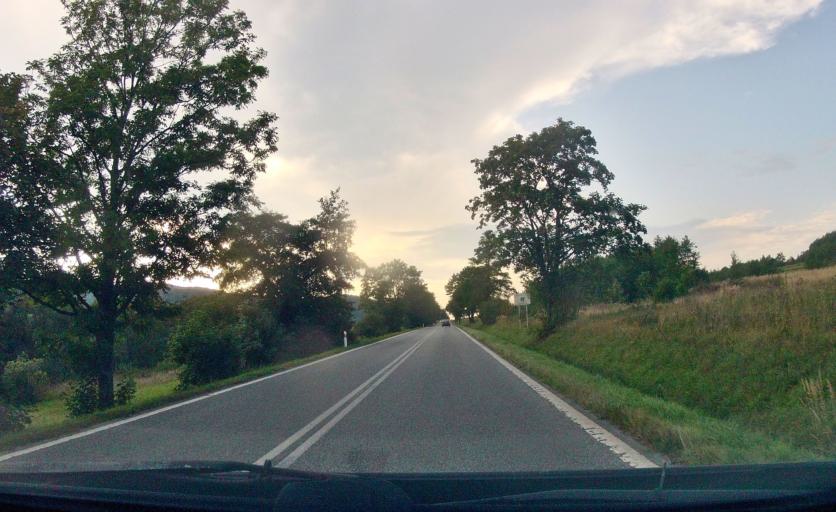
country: PL
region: Subcarpathian Voivodeship
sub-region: Powiat jasielski
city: Nowy Zmigrod
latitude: 49.5653
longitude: 21.5889
